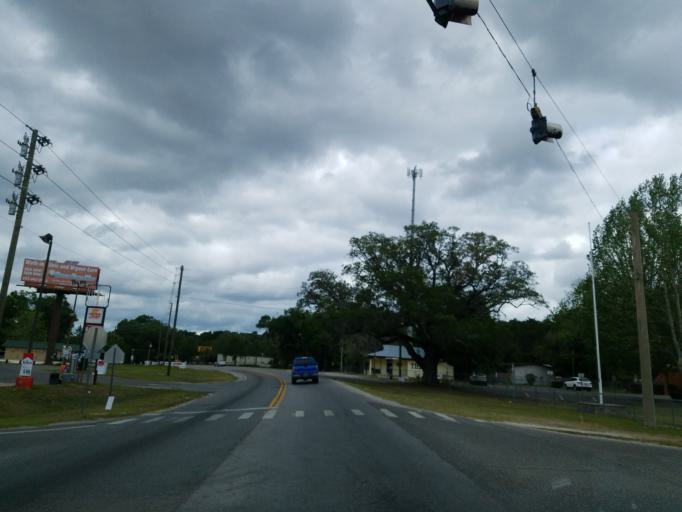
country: US
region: Florida
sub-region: Marion County
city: Ocala
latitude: 29.2884
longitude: -82.1116
